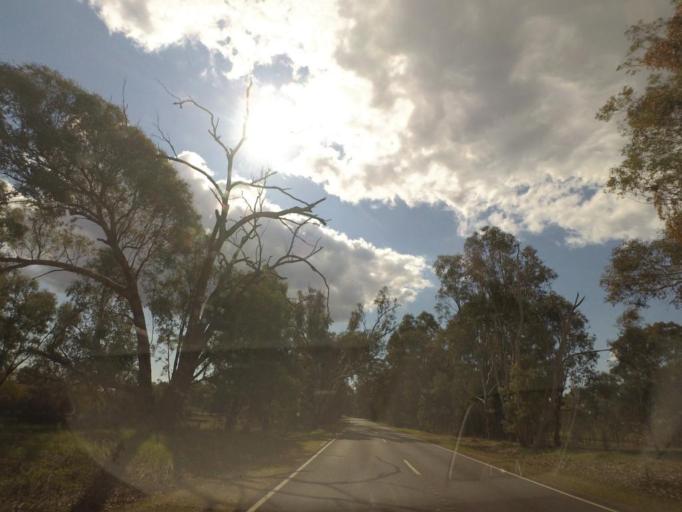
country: AU
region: New South Wales
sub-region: Corowa Shire
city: Howlong
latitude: -36.1731
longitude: 146.6078
